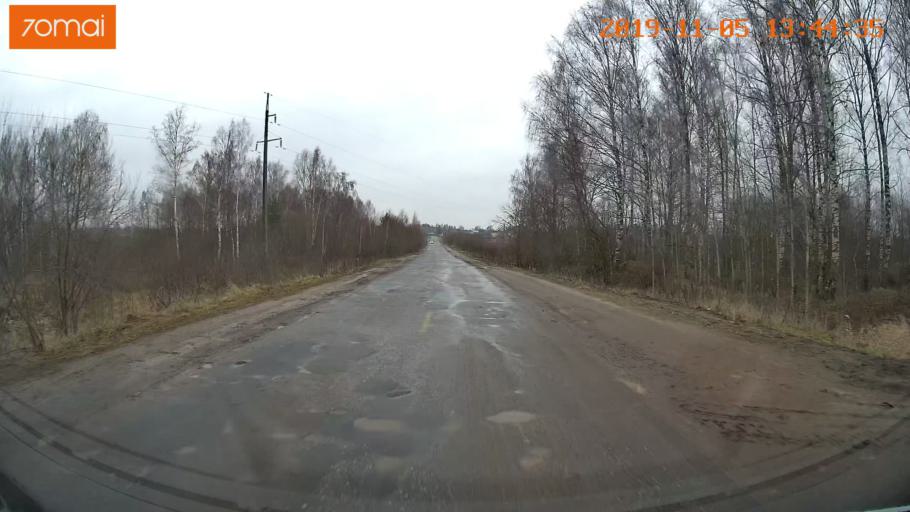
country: RU
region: Ivanovo
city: Shuya
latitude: 56.9821
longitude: 41.4110
